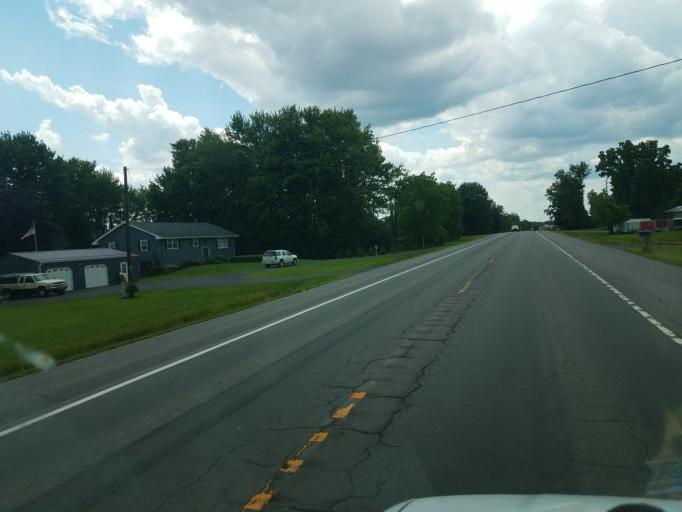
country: US
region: New York
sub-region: Seneca County
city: Waterloo
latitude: 42.9606
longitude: -76.8556
